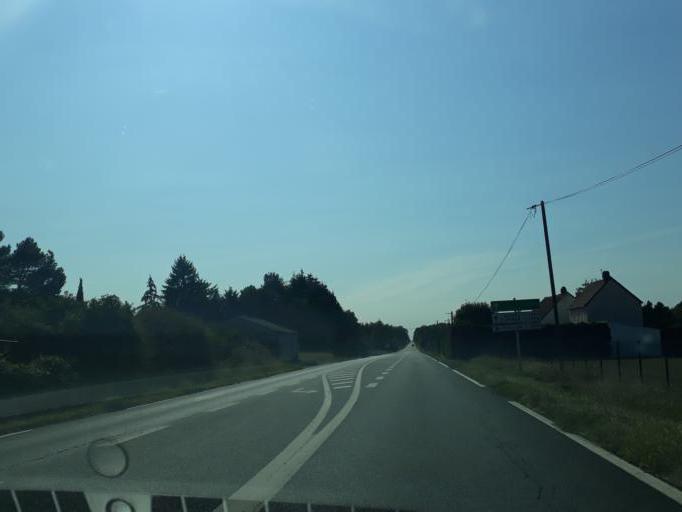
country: FR
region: Centre
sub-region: Departement du Loir-et-Cher
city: Chatillon-sur-Cher
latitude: 47.2833
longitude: 1.4944
